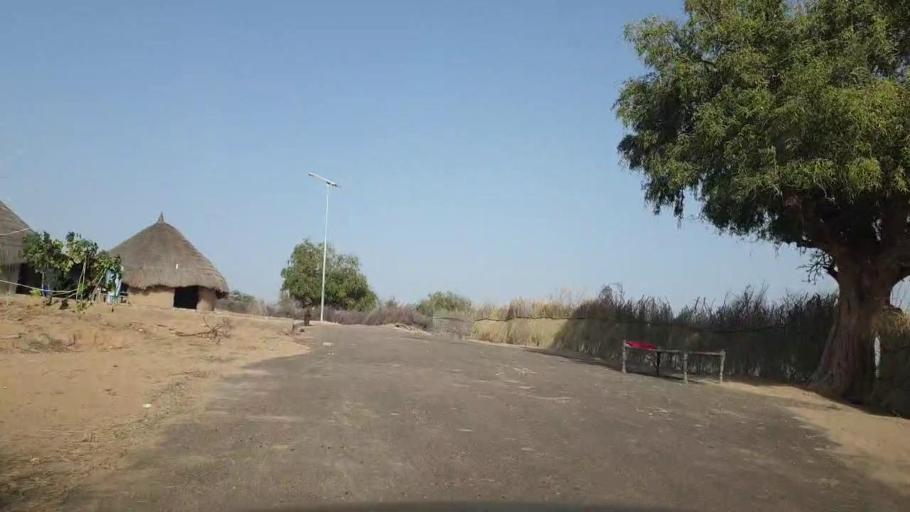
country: PK
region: Sindh
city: Islamkot
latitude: 25.1618
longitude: 70.5309
